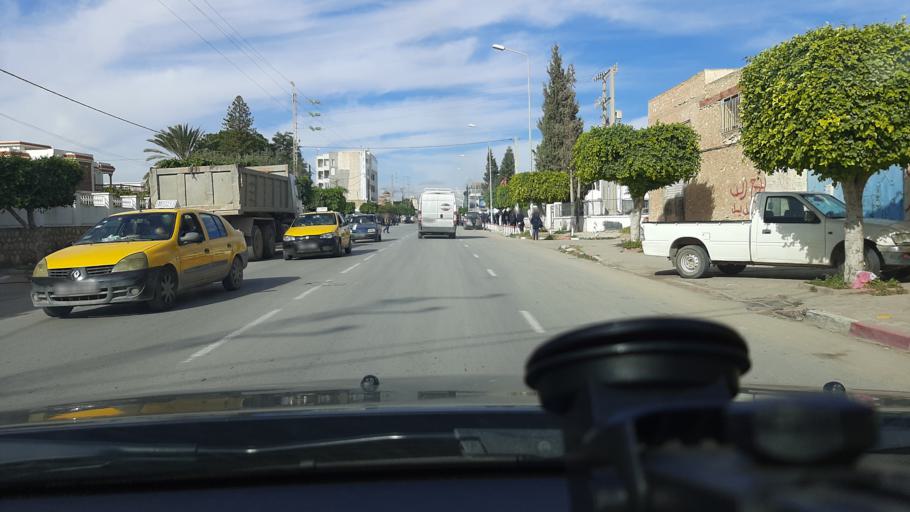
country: TN
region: Safaqis
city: Sfax
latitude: 34.7688
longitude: 10.7343
